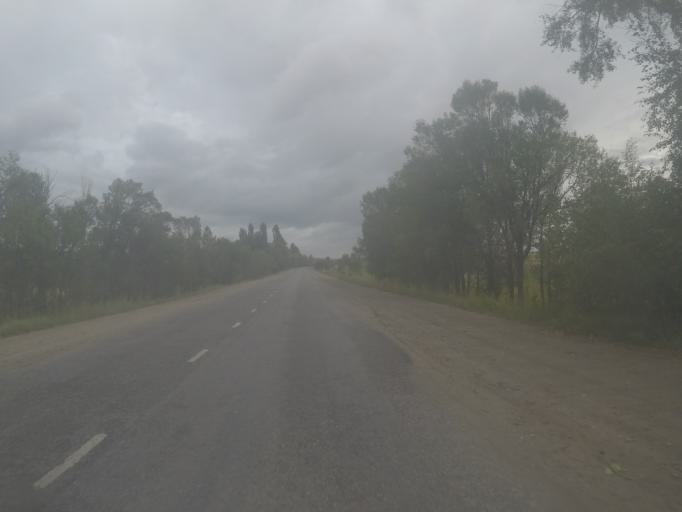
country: KG
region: Ysyk-Koel
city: Tyup
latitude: 42.6851
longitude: 78.3607
